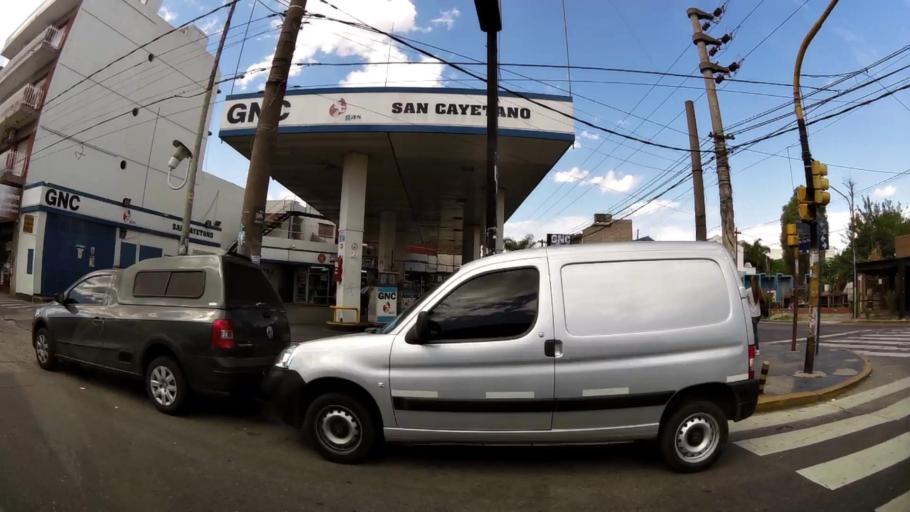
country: AR
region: Buenos Aires
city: San Justo
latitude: -34.6600
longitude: -58.5435
